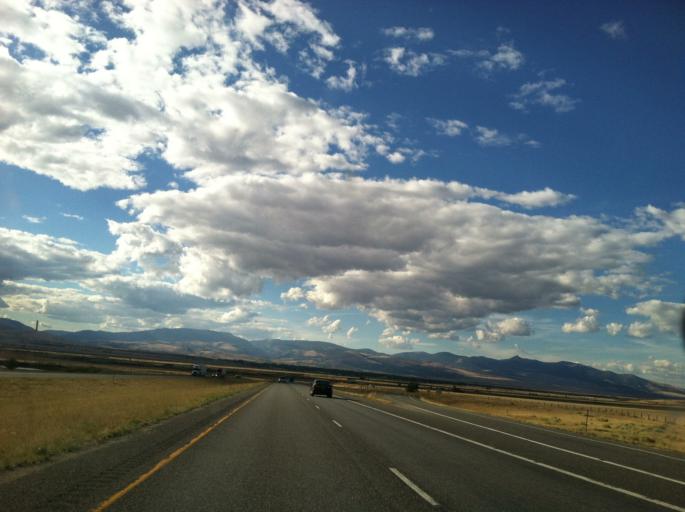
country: US
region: Montana
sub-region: Deer Lodge County
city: Warm Springs
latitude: 46.0685
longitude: -112.7786
